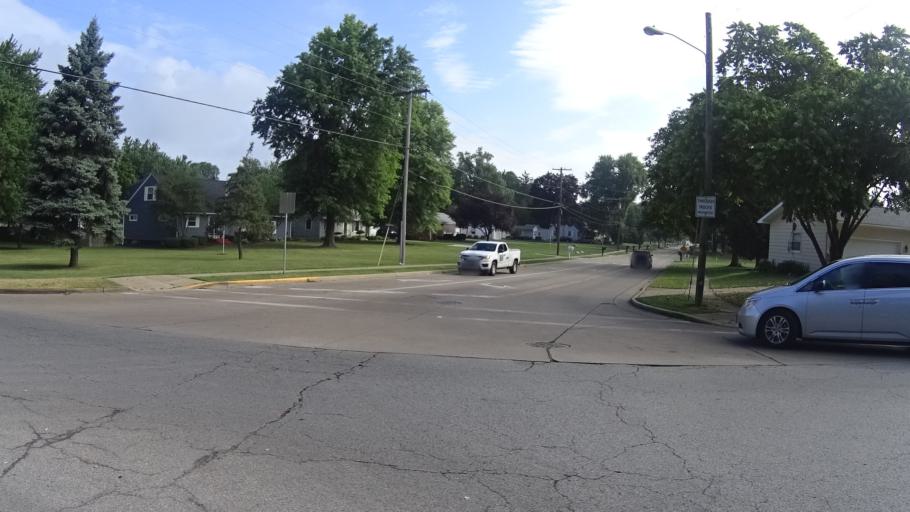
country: US
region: Ohio
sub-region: Erie County
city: Sandusky
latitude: 41.4324
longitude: -82.6784
